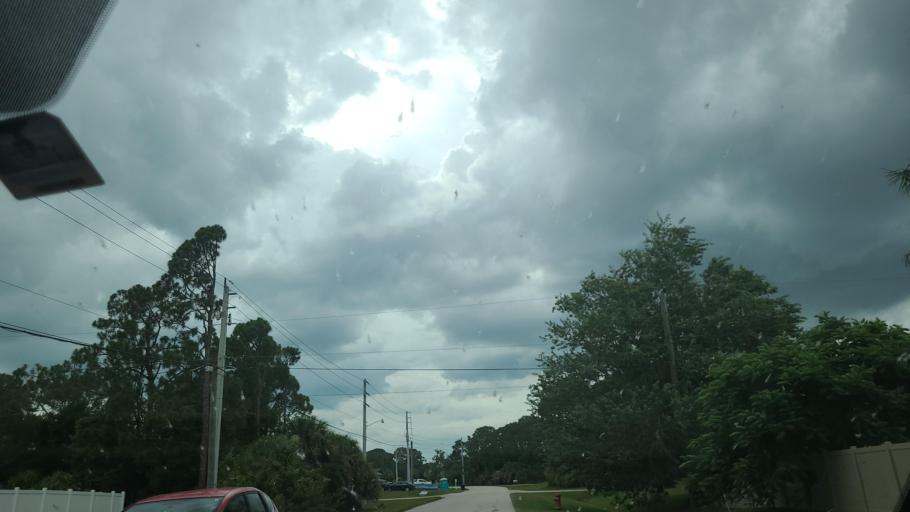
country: US
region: Florida
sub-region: Saint Lucie County
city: Port Saint Lucie
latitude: 27.2490
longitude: -80.4057
